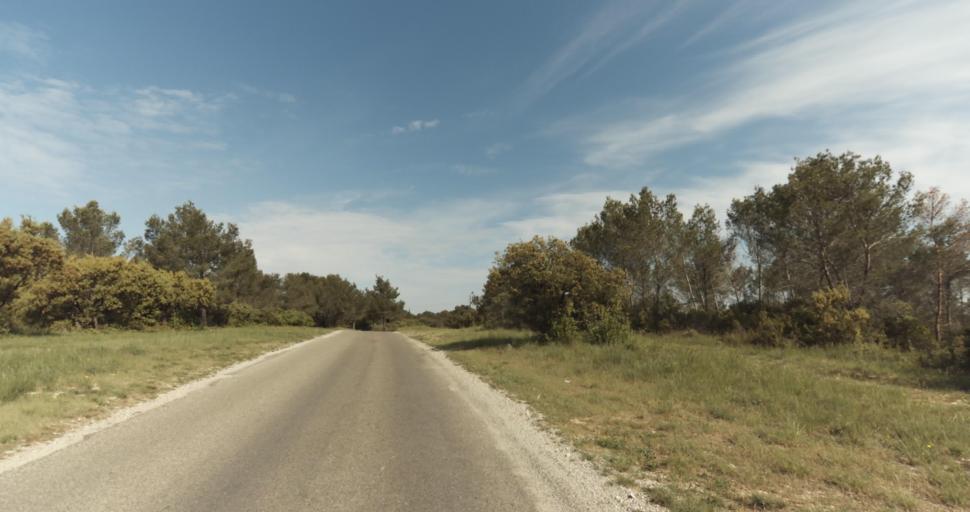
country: FR
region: Languedoc-Roussillon
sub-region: Departement du Gard
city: Poulx
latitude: 43.8791
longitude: 4.3899
